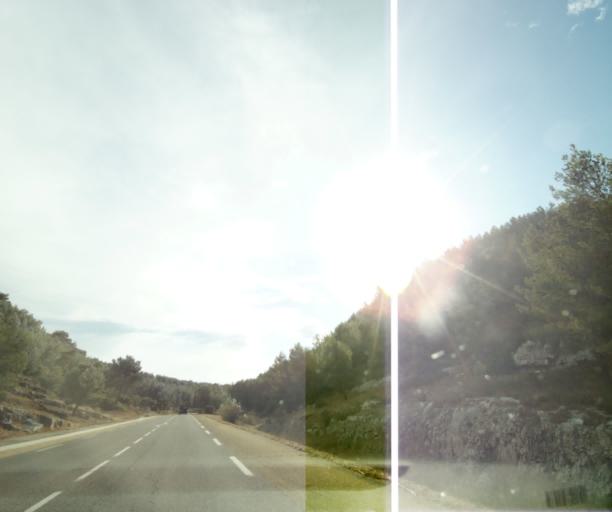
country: FR
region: Provence-Alpes-Cote d'Azur
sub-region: Departement des Bouches-du-Rhone
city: Sausset-les-Pins
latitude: 43.3548
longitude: 5.1039
